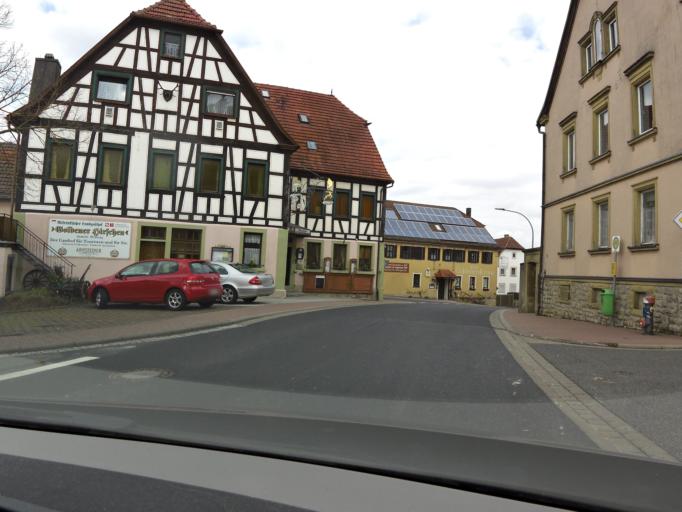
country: DE
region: Bavaria
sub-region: Regierungsbezirk Unterfranken
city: Arnstein
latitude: 49.9275
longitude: 9.9704
